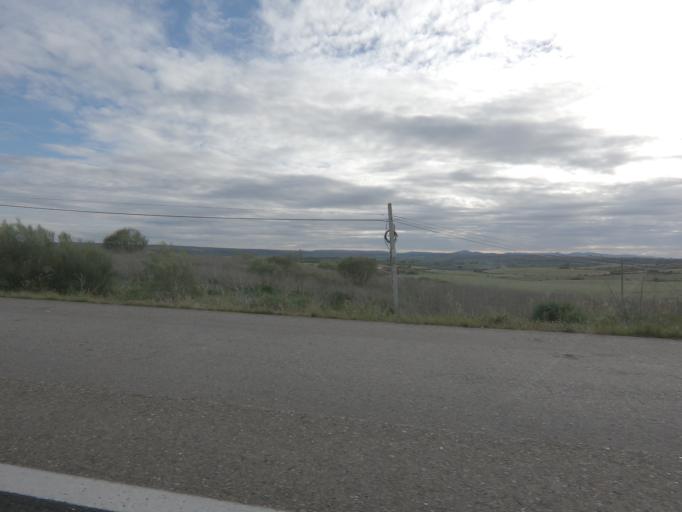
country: ES
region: Extremadura
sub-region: Provincia de Caceres
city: Coria
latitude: 40.0081
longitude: -6.5596
